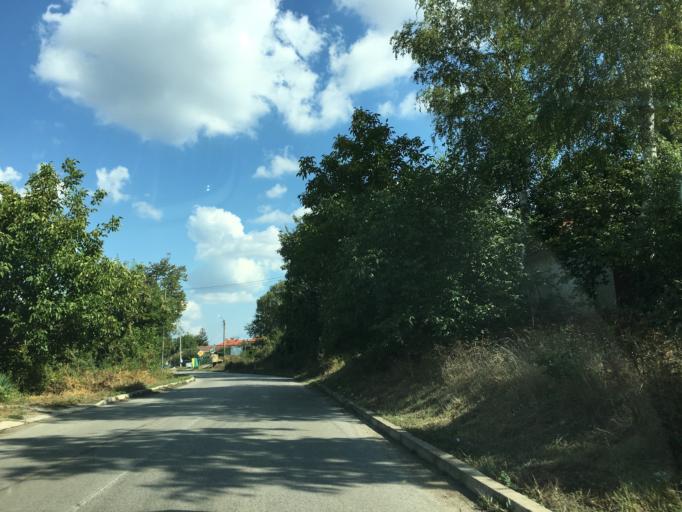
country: BG
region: Montana
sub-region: Obshtina Lom
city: Lom
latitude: 43.8257
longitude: 23.2115
